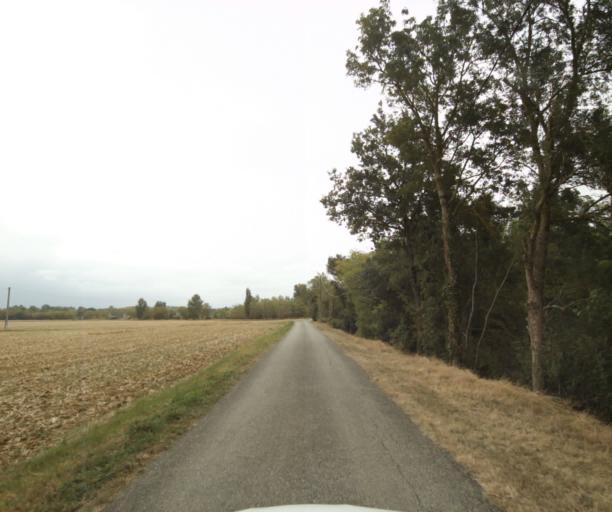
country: FR
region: Midi-Pyrenees
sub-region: Departement de la Haute-Garonne
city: Villefranche-de-Lauragais
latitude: 43.3945
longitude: 1.7032
